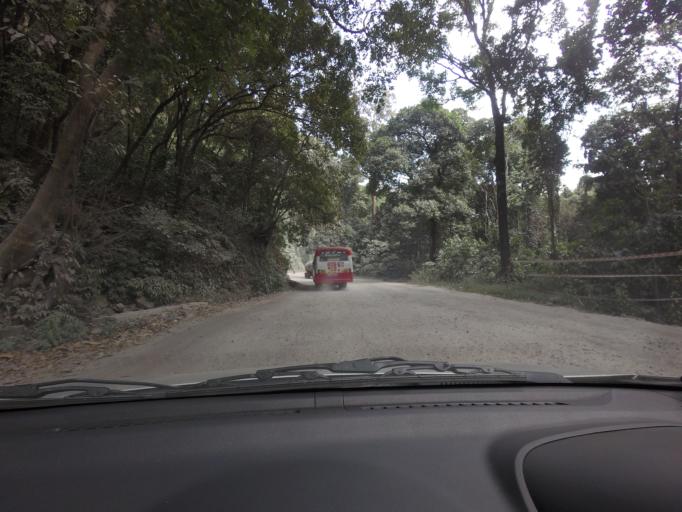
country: IN
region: Karnataka
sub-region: Hassan
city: Sakleshpur
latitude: 12.8287
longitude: 75.6002
